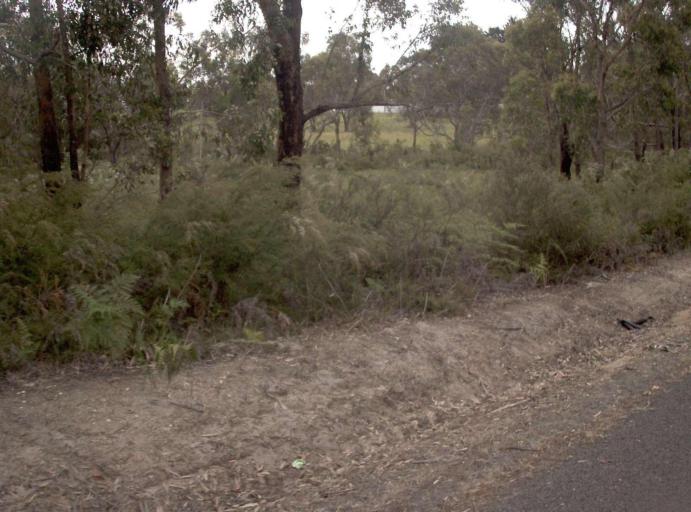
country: AU
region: Victoria
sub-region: Wellington
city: Sale
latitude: -38.3289
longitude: 147.0180
